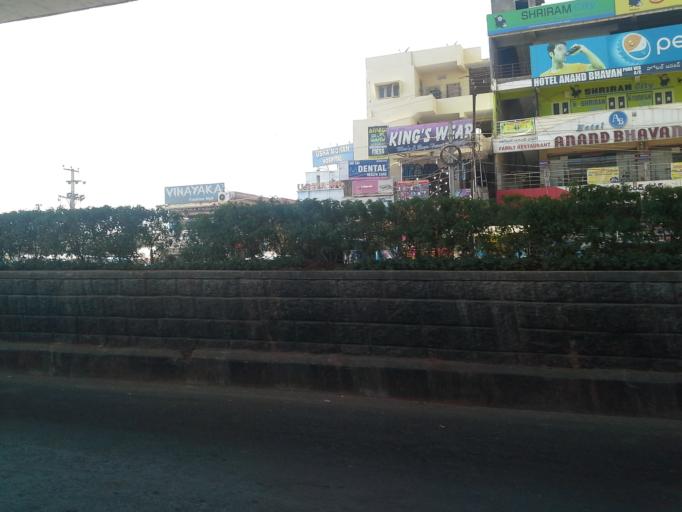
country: IN
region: Telangana
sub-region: Hyderabad
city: Hyderabad
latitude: 17.3643
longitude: 78.4283
